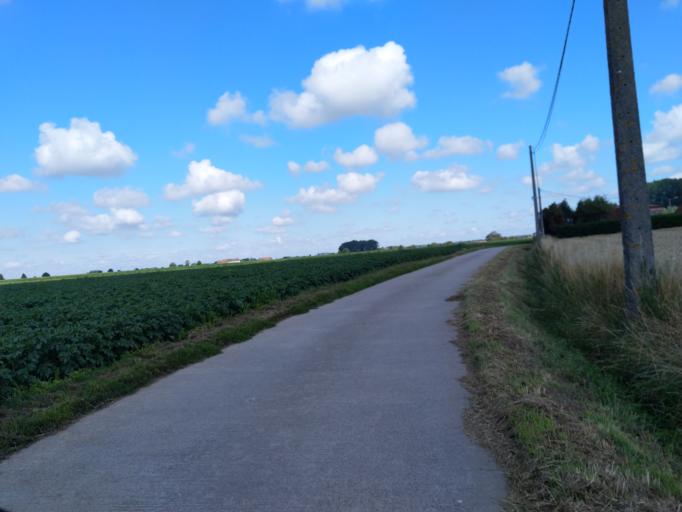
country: BE
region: Wallonia
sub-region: Province du Hainaut
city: Chievres
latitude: 50.5659
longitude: 3.8153
